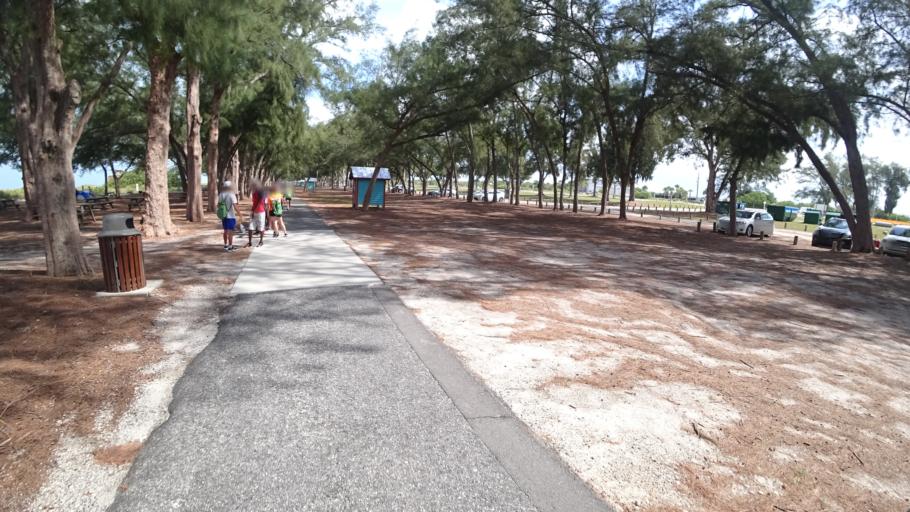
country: US
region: Florida
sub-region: Manatee County
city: Cortez
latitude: 27.4479
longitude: -82.6911
